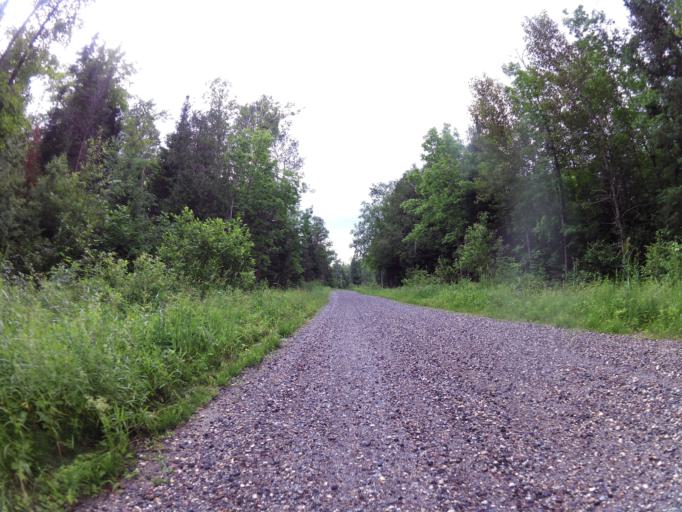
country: CA
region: Ontario
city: Renfrew
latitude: 45.0763
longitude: -76.7360
